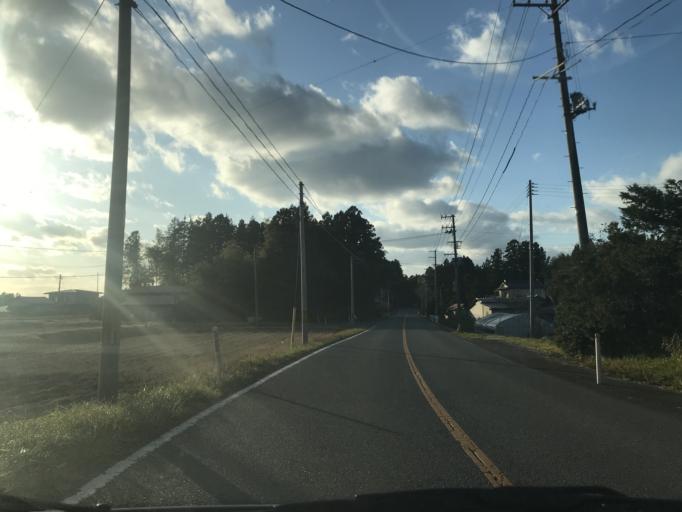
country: JP
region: Miyagi
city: Wakuya
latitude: 38.6699
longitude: 141.1016
